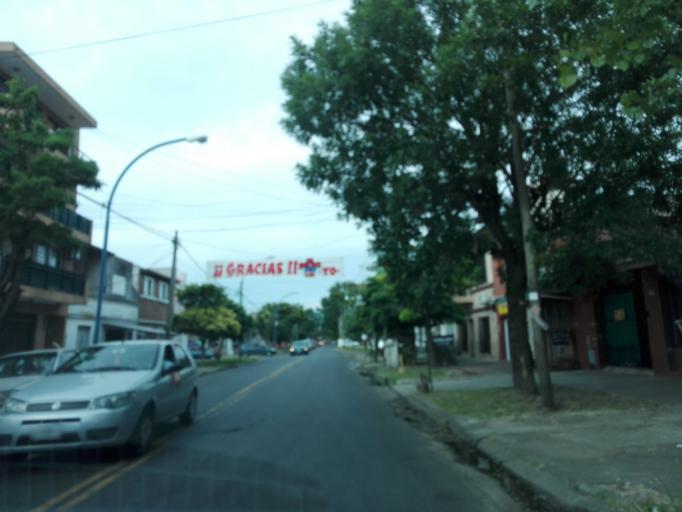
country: AR
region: Buenos Aires
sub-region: Partido de Lanus
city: Lanus
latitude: -34.7086
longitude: -58.3738
